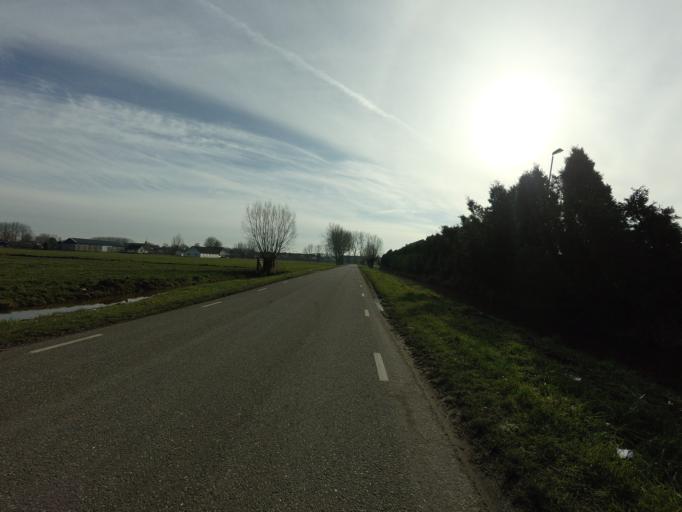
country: NL
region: South Holland
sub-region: Gemeente Hardinxveld-Giessendam
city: Neder-Hardinxveld
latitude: 51.8326
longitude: 4.8265
